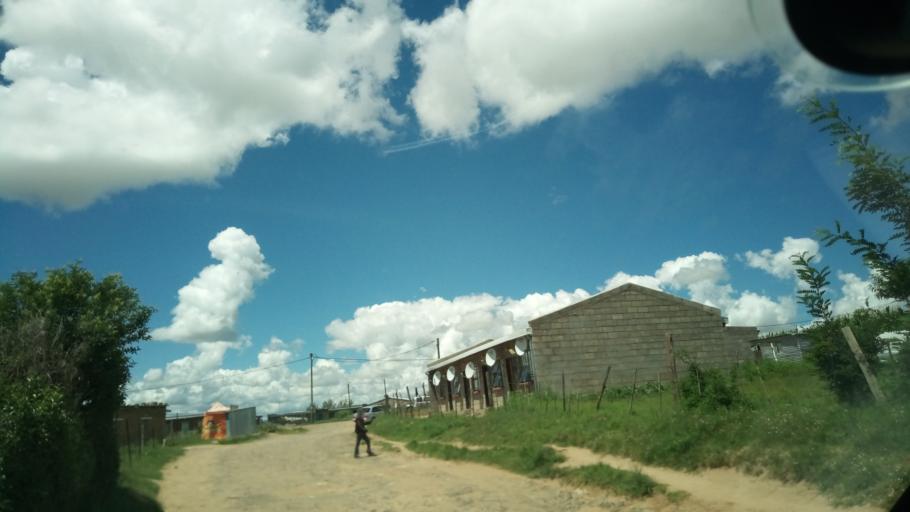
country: LS
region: Maseru
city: Maseru
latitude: -29.3655
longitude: 27.5412
